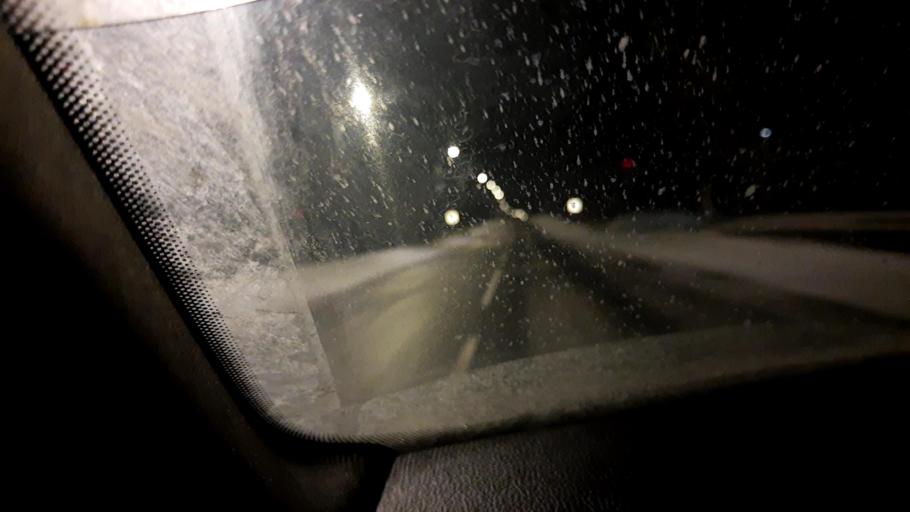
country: RU
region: Moskovskaya
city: Bogorodskoye
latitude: 56.5865
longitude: 38.1535
